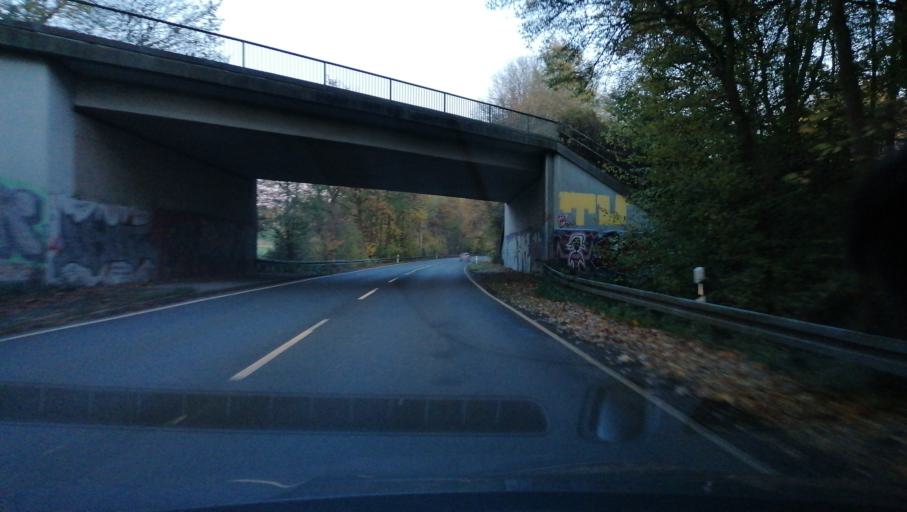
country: DE
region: North Rhine-Westphalia
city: Herdecke
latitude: 51.4144
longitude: 7.4191
